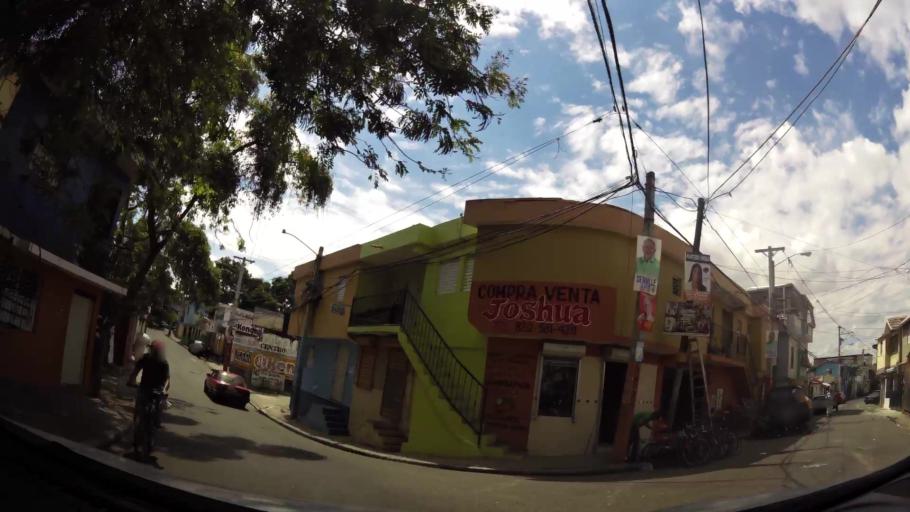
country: DO
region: Santiago
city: Santiago de los Caballeros
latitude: 19.4670
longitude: -70.7011
